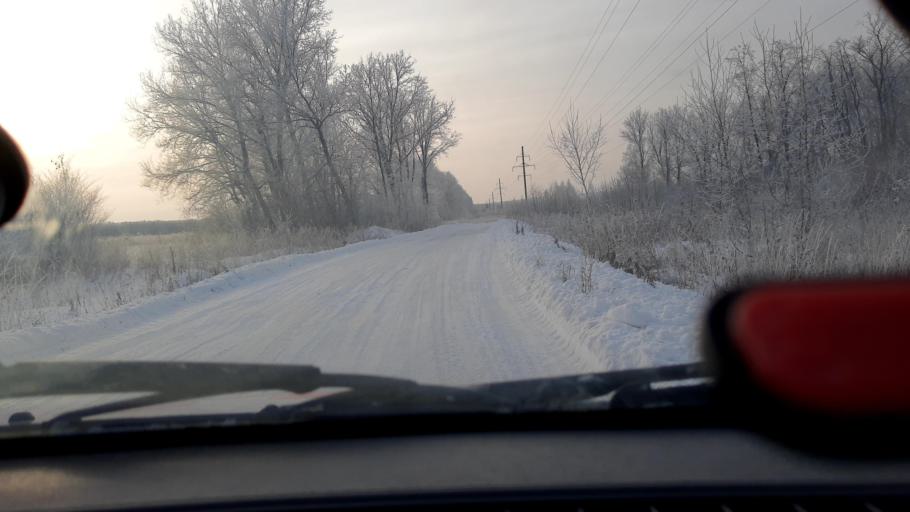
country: RU
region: Bashkortostan
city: Iglino
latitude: 54.7327
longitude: 56.2391
